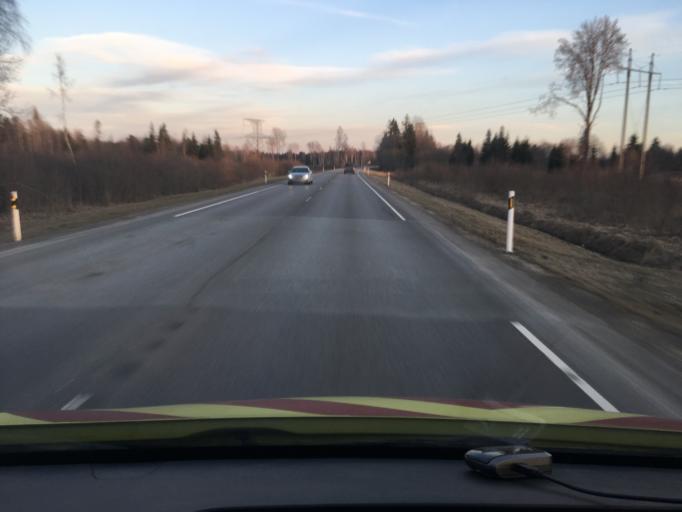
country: EE
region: Raplamaa
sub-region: Kohila vald
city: Kohila
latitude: 59.2352
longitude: 24.7673
